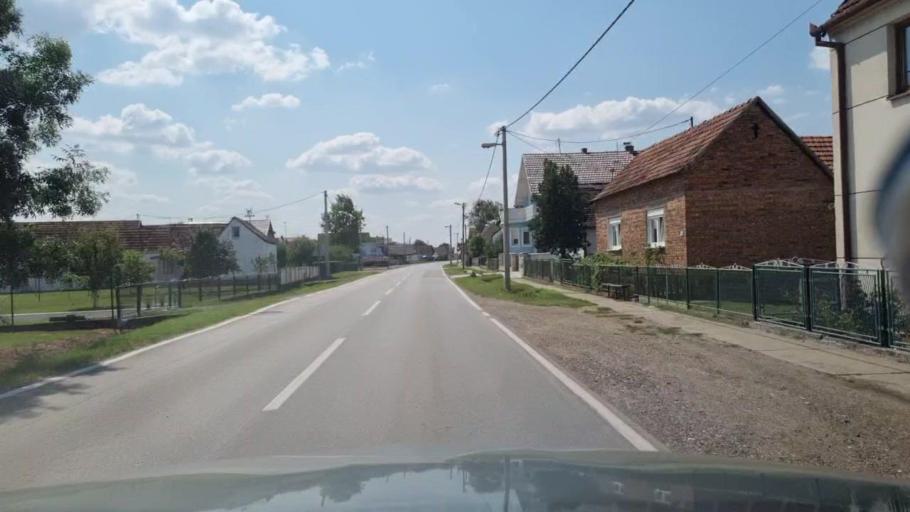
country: BA
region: Federation of Bosnia and Herzegovina
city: Donja Mahala
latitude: 45.0468
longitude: 18.6707
